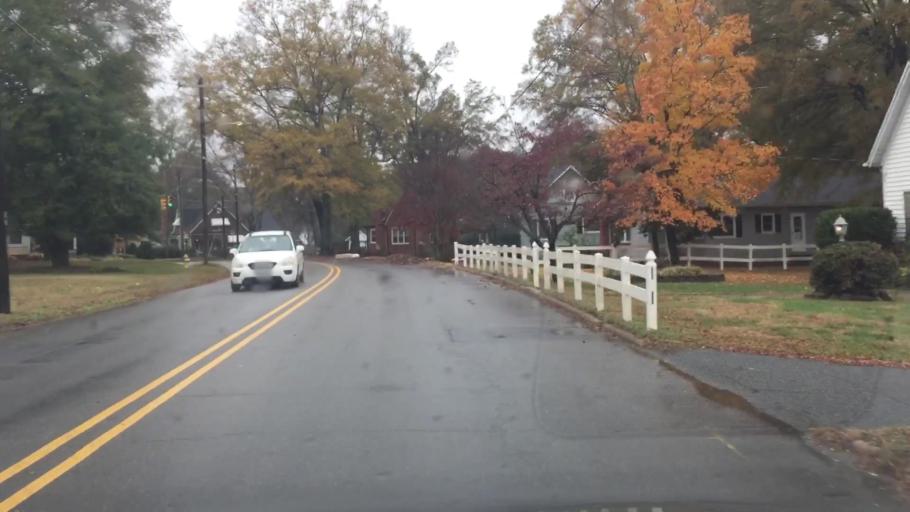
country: US
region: North Carolina
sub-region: Iredell County
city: Mooresville
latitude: 35.5823
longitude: -80.7985
